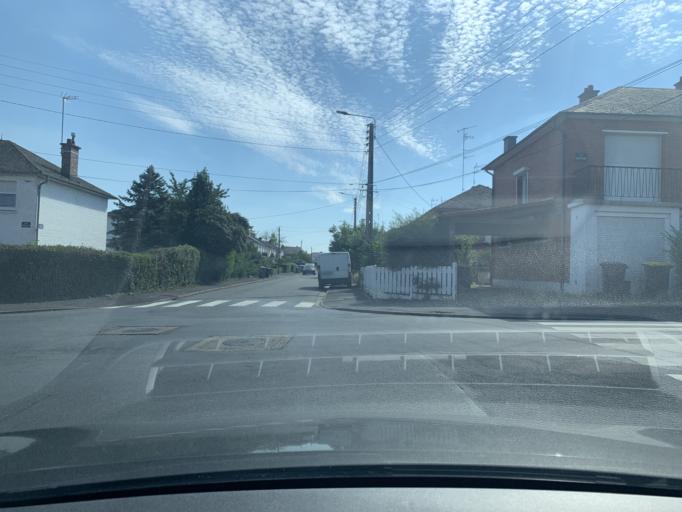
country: FR
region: Nord-Pas-de-Calais
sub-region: Departement du Nord
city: Cambrai
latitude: 50.1621
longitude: 3.2339
